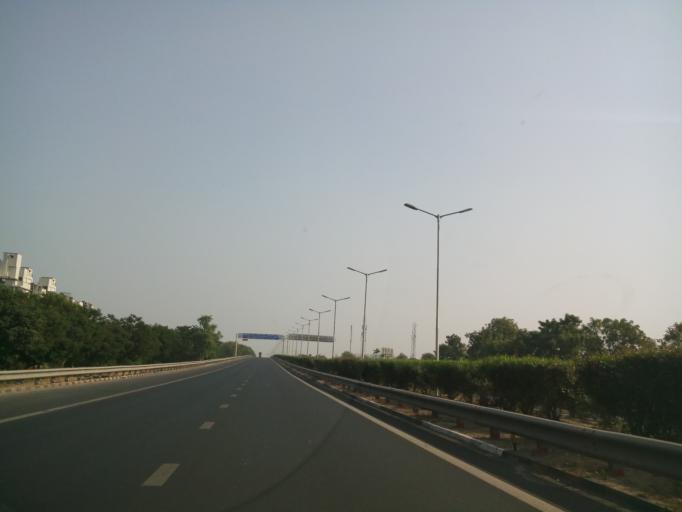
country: IN
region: Gujarat
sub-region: Ahmadabad
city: Ahmedabad
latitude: 22.9827
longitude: 72.6385
